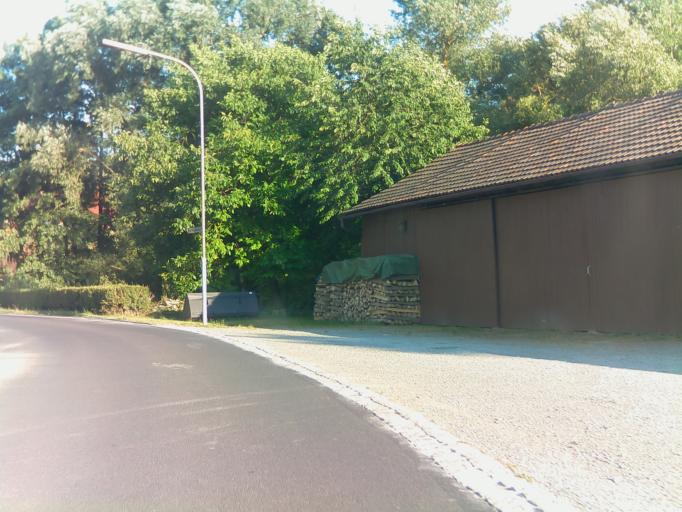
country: DE
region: Bavaria
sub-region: Regierungsbezirk Unterfranken
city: Mellrichstadt
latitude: 50.4465
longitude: 10.3413
